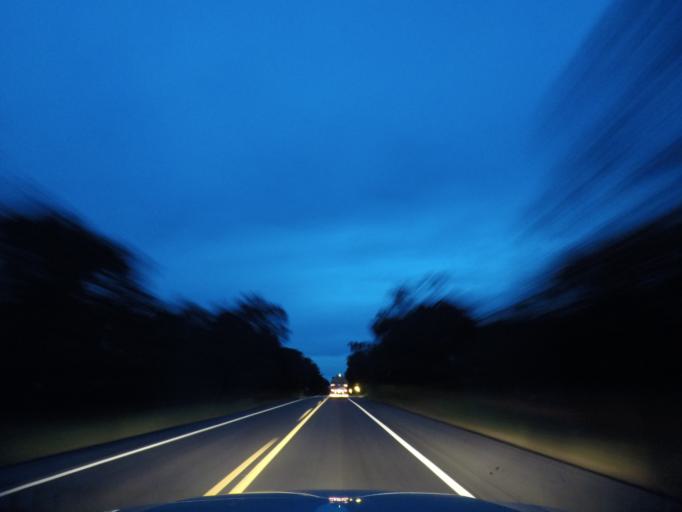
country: BR
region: Bahia
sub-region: Andarai
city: Vera Cruz
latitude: -12.4826
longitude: -41.3508
